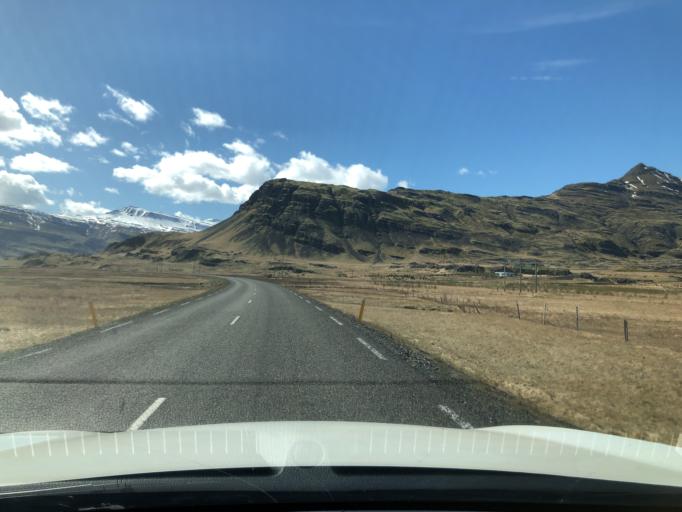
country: IS
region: East
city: Reydarfjoerdur
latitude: 64.5839
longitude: -14.5826
